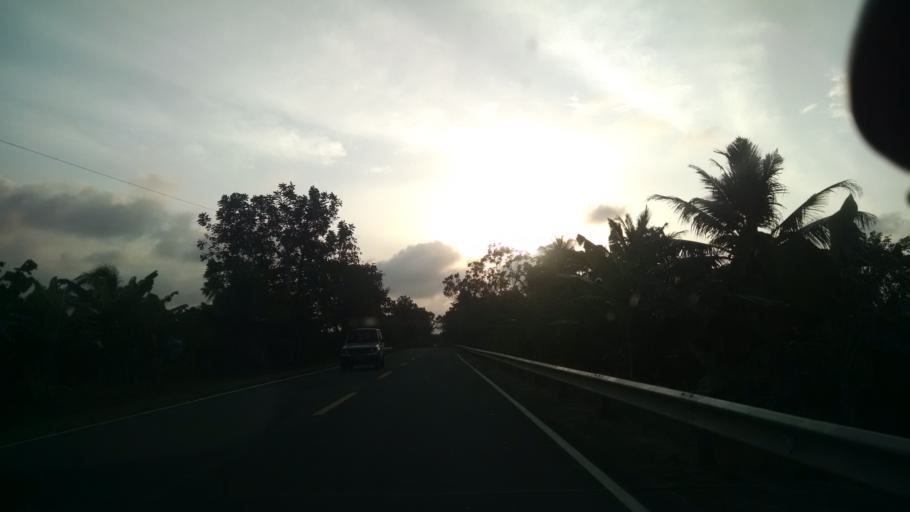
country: CO
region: Antioquia
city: San Juan de Uraba
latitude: 8.7259
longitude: -76.5892
